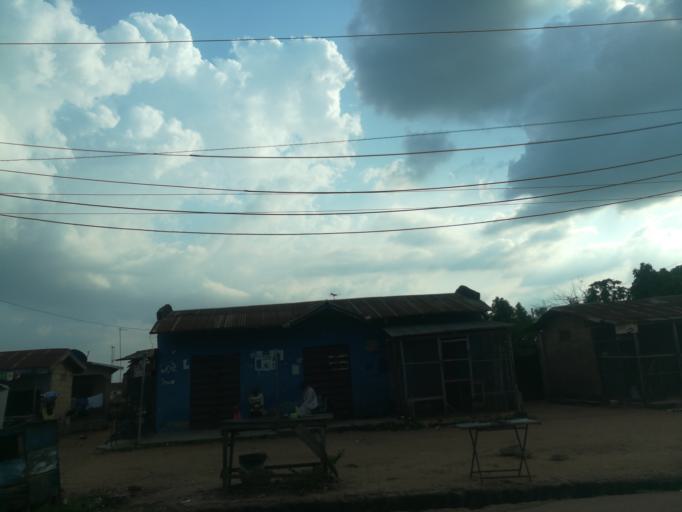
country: NG
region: Oyo
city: Moniya
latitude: 7.4800
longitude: 3.9086
